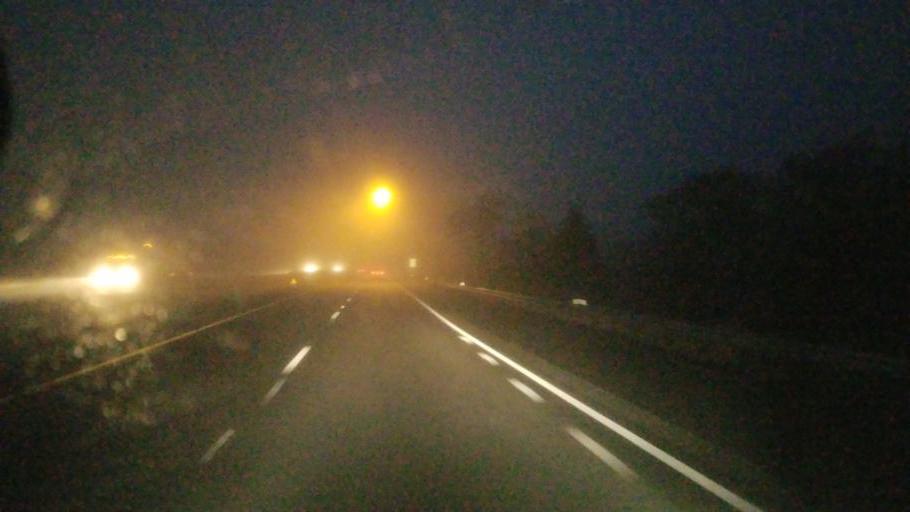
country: US
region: Ohio
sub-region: Ross County
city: Chillicothe
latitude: 39.3827
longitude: -82.9693
